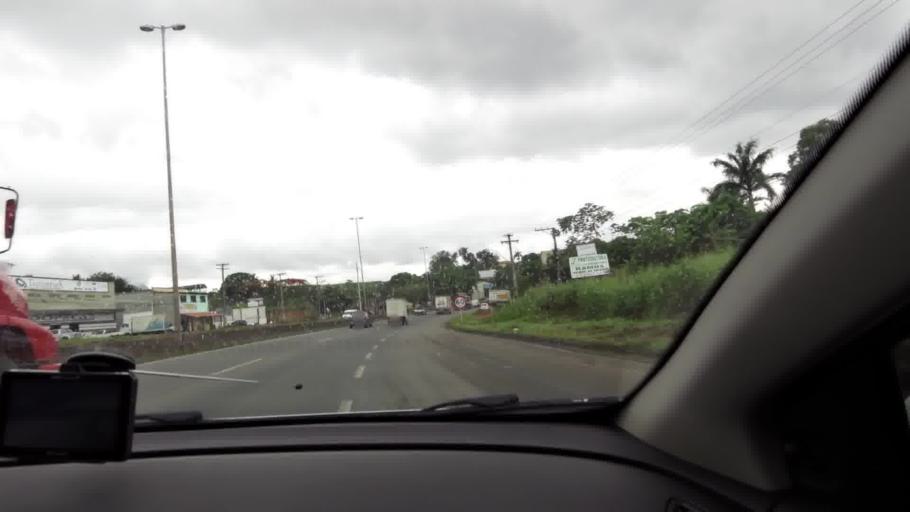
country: BR
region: Espirito Santo
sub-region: Viana
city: Viana
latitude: -20.3634
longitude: -40.4424
